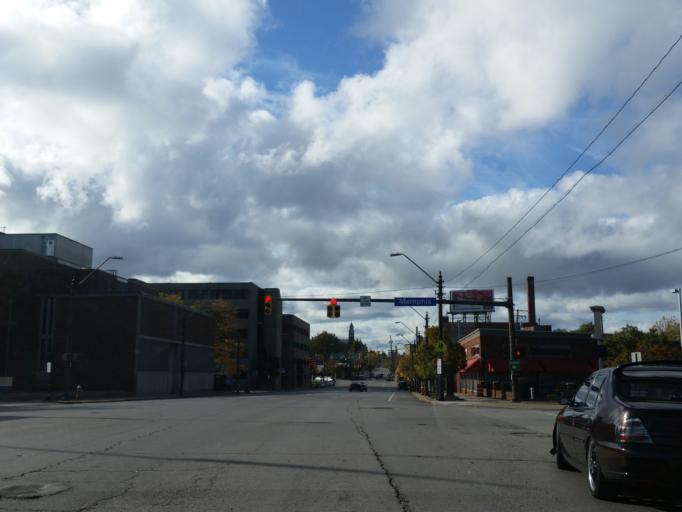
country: US
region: Ohio
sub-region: Cuyahoga County
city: Brooklyn Heights
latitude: 41.4409
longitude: -81.7055
